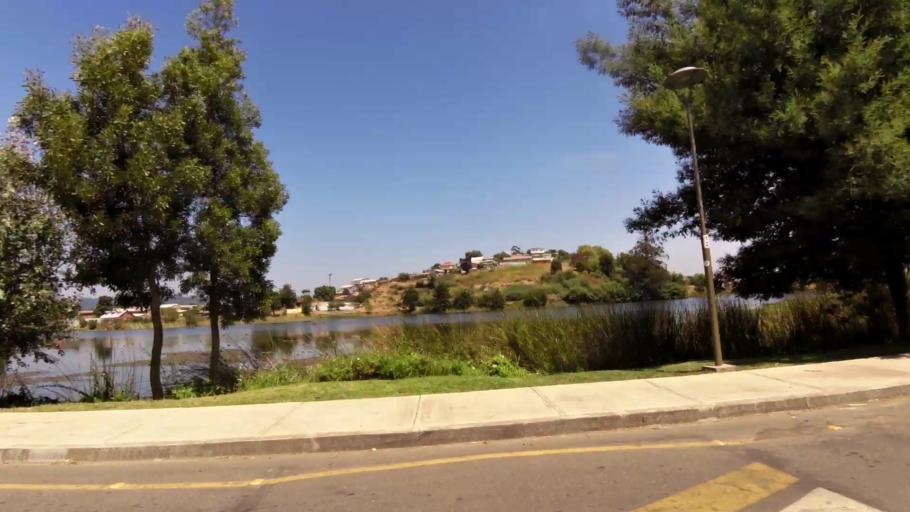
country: CL
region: Biobio
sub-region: Provincia de Concepcion
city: Concepcion
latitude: -36.7999
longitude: -73.0508
